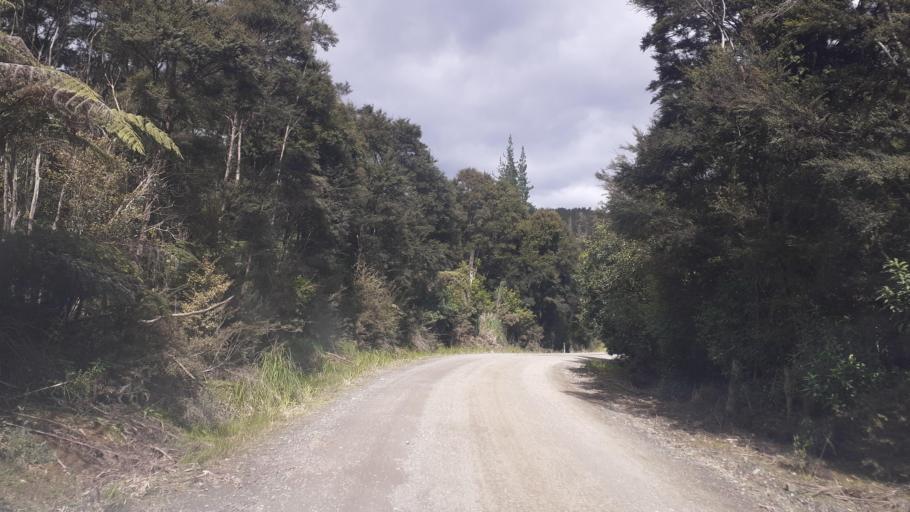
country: NZ
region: Northland
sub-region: Far North District
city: Moerewa
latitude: -35.5825
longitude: 173.9418
